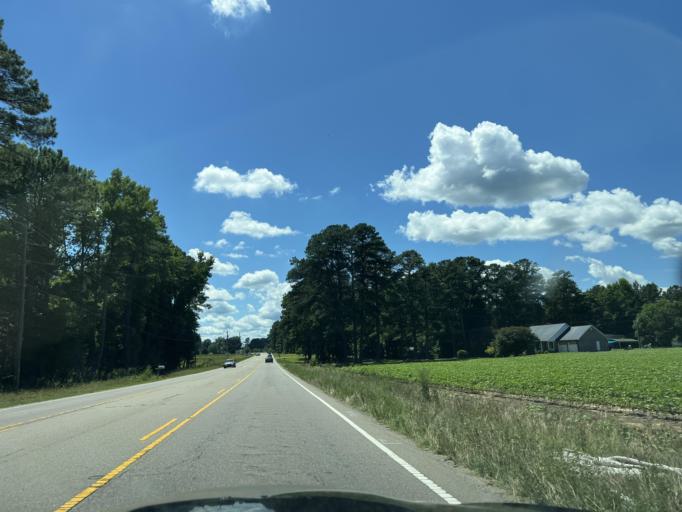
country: US
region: North Carolina
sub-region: Lee County
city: Sanford
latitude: 35.4380
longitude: -79.2051
